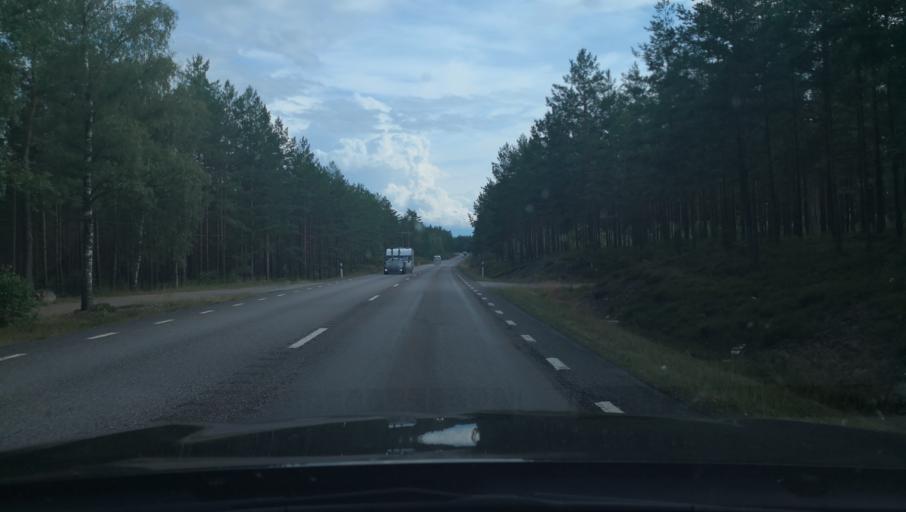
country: SE
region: Kalmar
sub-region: Vimmerby Kommun
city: Sodra Vi
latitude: 57.7458
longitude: 15.7748
